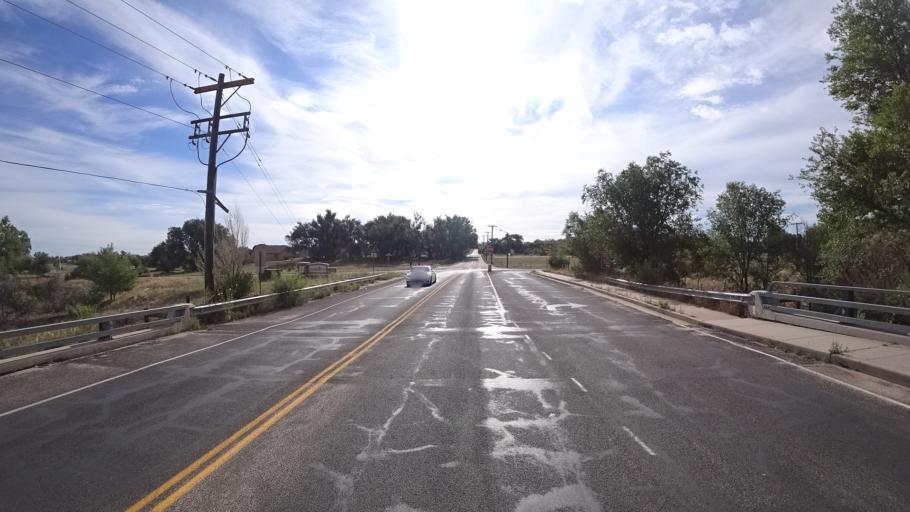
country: US
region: Colorado
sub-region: El Paso County
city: Fountain
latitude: 38.6840
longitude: -104.6882
